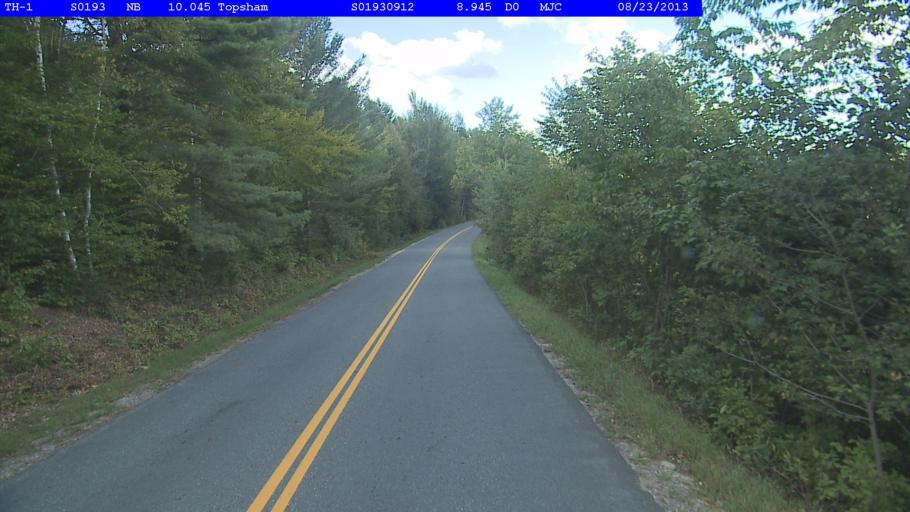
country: US
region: New Hampshire
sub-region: Grafton County
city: Woodsville
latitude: 44.1870
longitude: -72.2223
